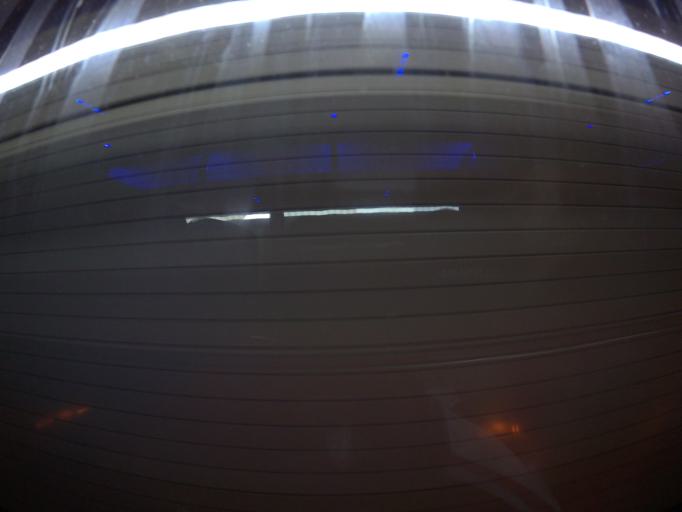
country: US
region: New Jersey
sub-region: Hudson County
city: Weehawken
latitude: 40.7687
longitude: -74.0205
